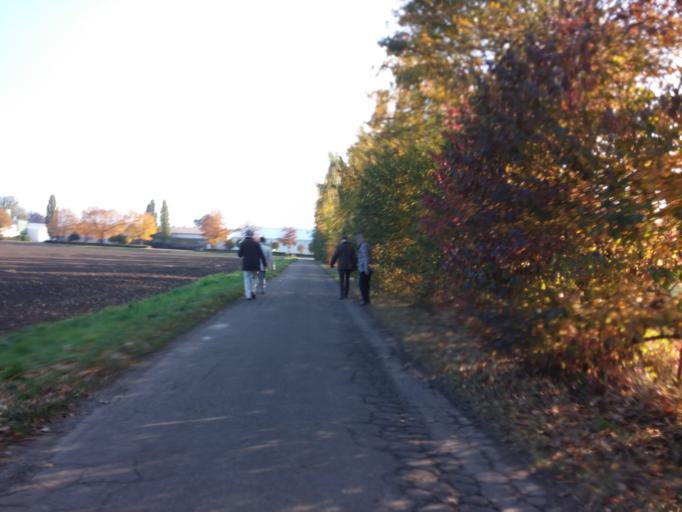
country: DE
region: North Rhine-Westphalia
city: Dorsten
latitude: 51.6379
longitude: 6.9841
